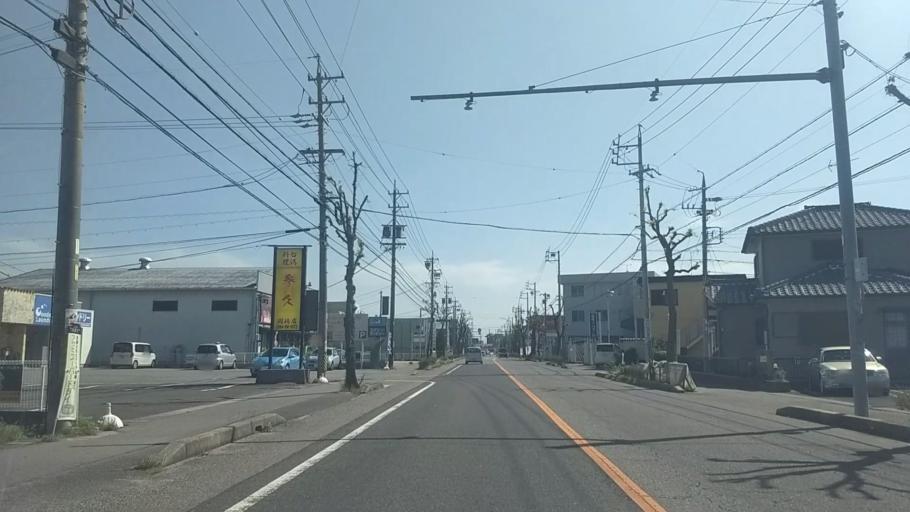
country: JP
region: Aichi
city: Okazaki
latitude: 34.9826
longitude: 137.1393
